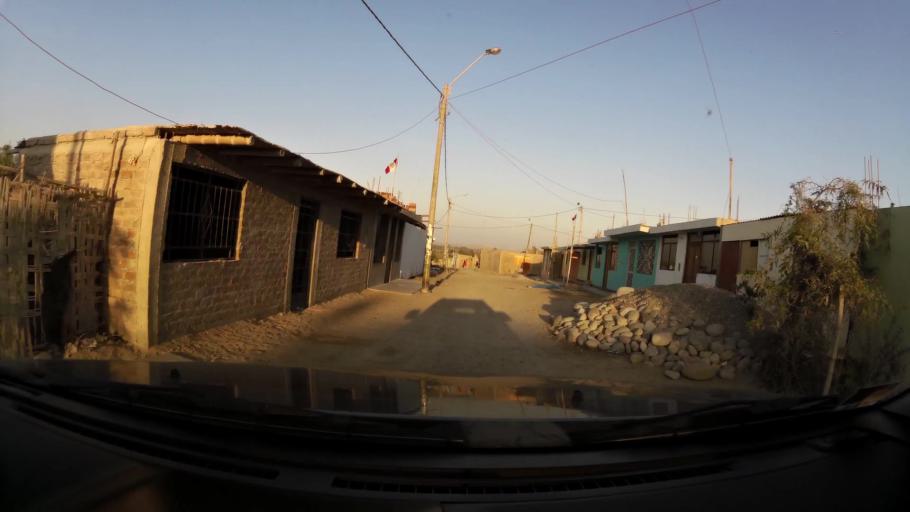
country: PE
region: Ica
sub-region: Provincia de Pisco
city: Villa Tupac Amaru
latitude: -13.6991
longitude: -76.1549
